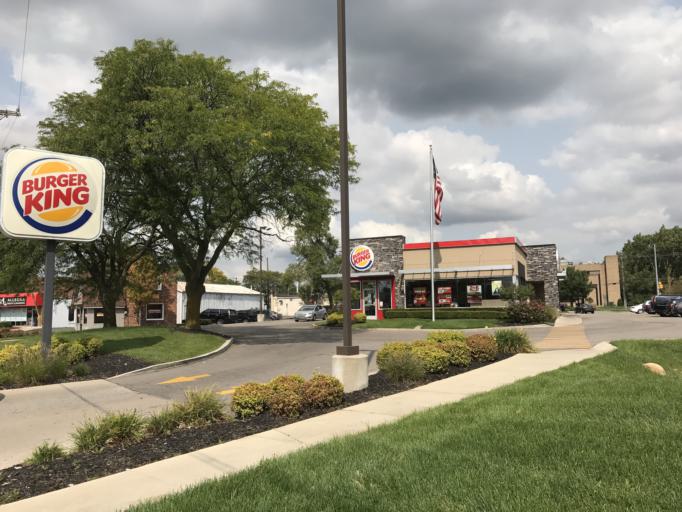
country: US
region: Michigan
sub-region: Oakland County
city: Franklin
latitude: 42.4998
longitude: -83.3051
